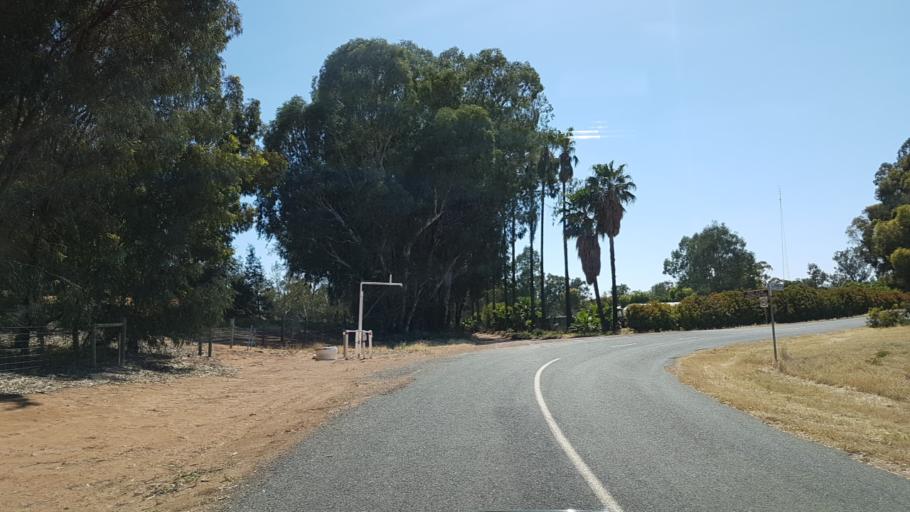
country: AU
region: South Australia
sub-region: Loxton Waikerie
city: Waikerie
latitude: -34.1644
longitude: 140.0312
